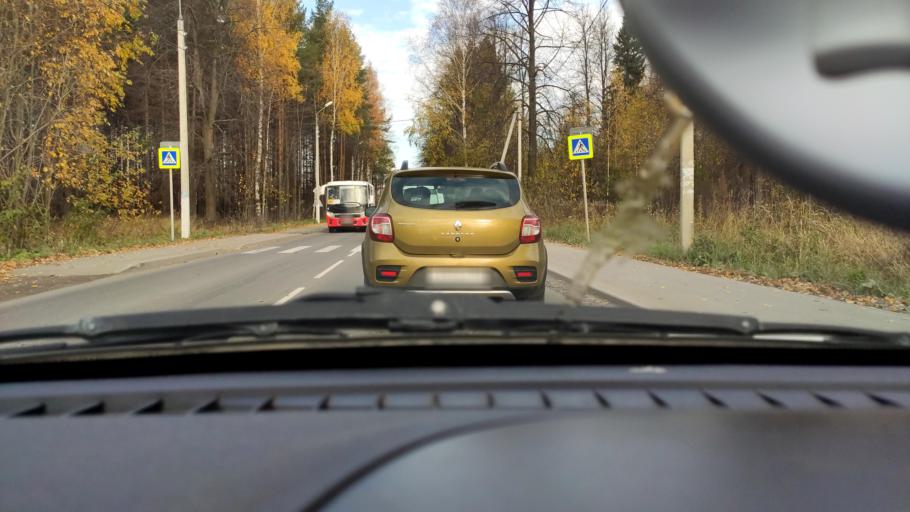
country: RU
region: Perm
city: Perm
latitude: 58.0922
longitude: 56.4041
